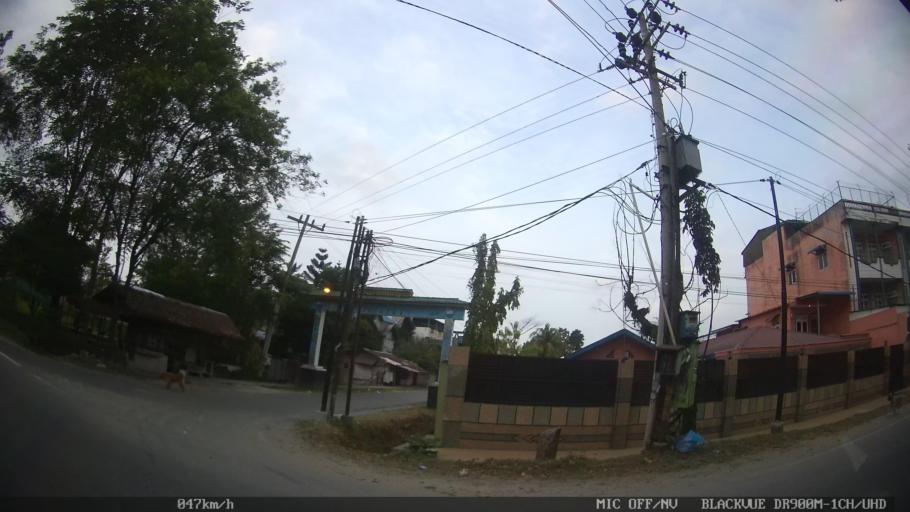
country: ID
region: North Sumatra
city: Sunggal
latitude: 3.5675
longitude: 98.6145
